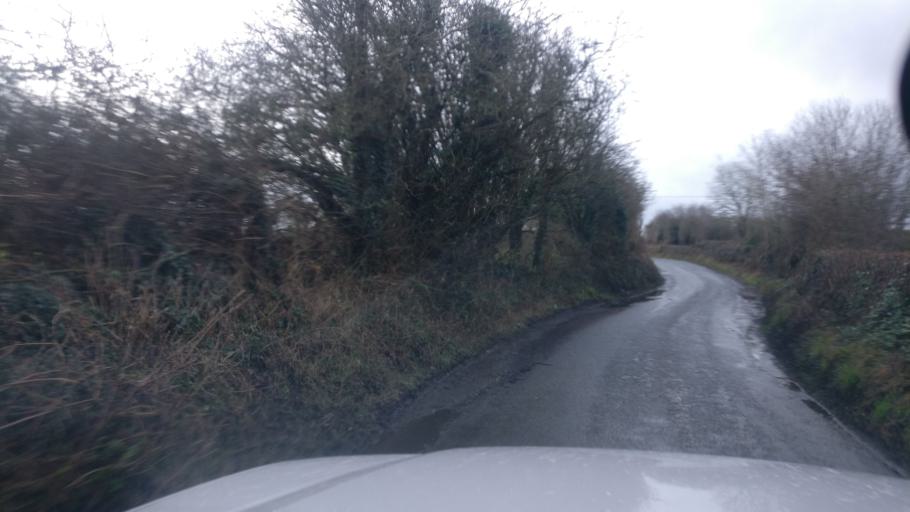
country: IE
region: Connaught
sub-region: County Galway
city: Athenry
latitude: 53.2611
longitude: -8.8000
